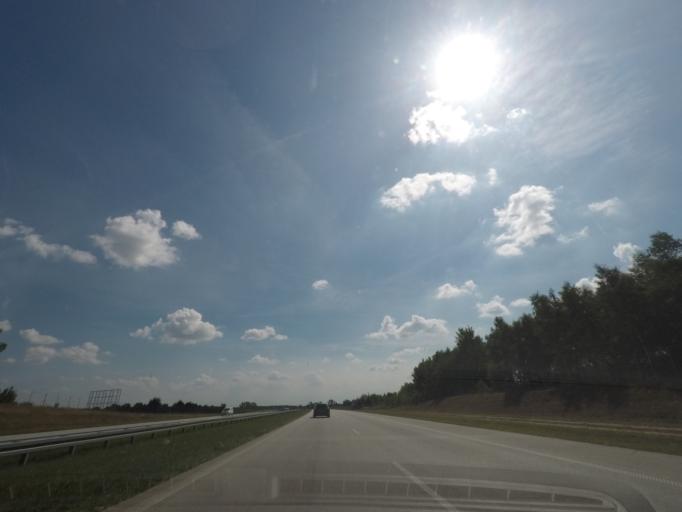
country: PL
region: Lodz Voivodeship
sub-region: Powiat lodzki wschodni
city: Andrespol
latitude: 51.7683
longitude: 19.5982
